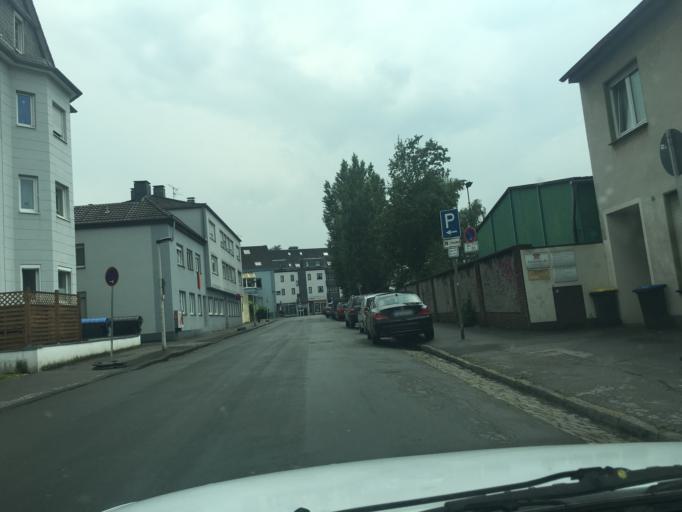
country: DE
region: North Rhine-Westphalia
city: Haan
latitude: 51.1619
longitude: 7.0058
